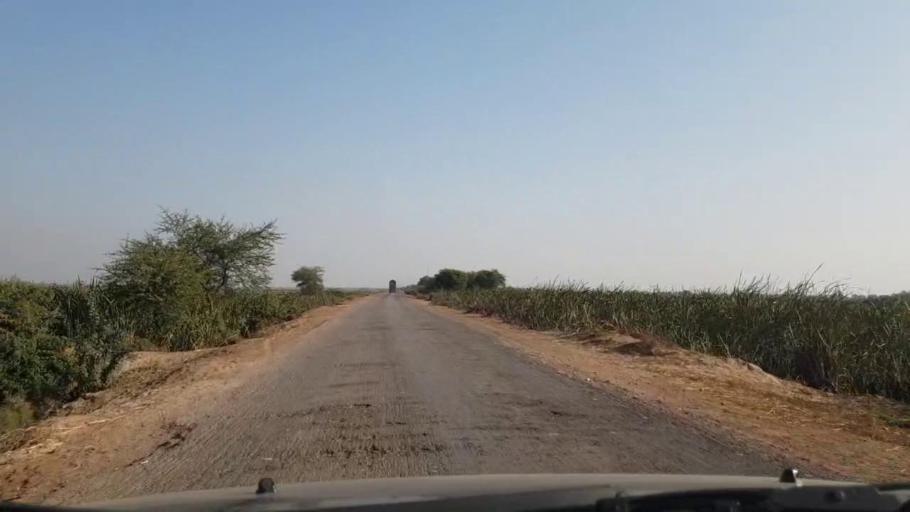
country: PK
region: Sindh
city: Tando Bago
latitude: 24.8311
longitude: 69.0171
